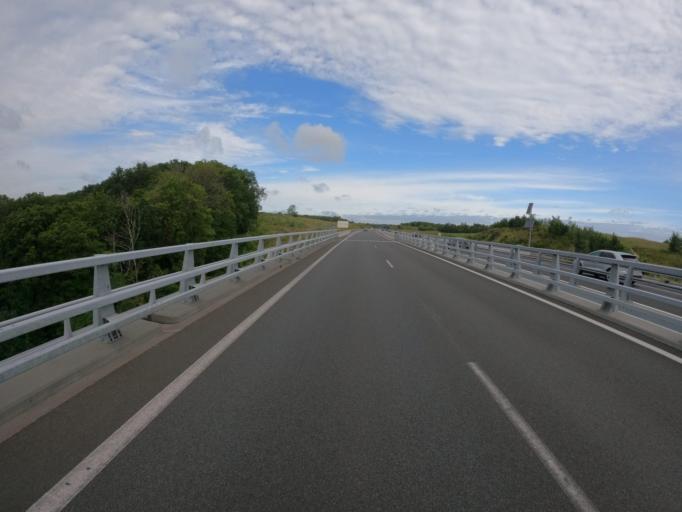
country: FR
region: Centre
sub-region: Departement d'Indre-et-Loire
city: Cinq-Mars-la-Pile
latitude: 47.3372
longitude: 0.4316
